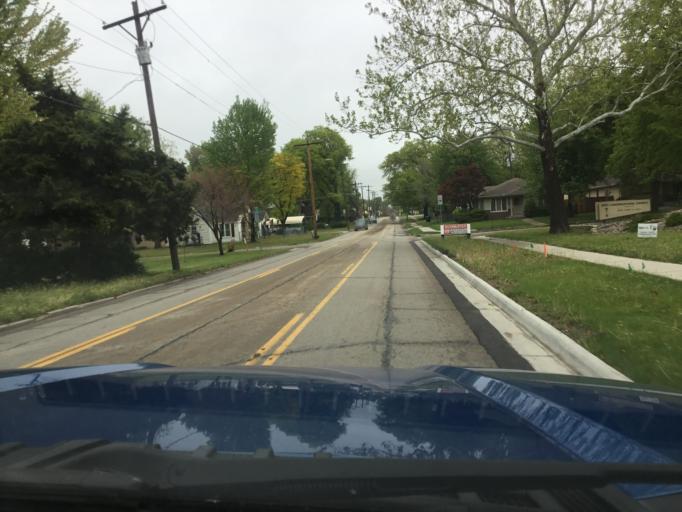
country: US
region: Kansas
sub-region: Shawnee County
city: Topeka
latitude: 39.0369
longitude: -95.7138
